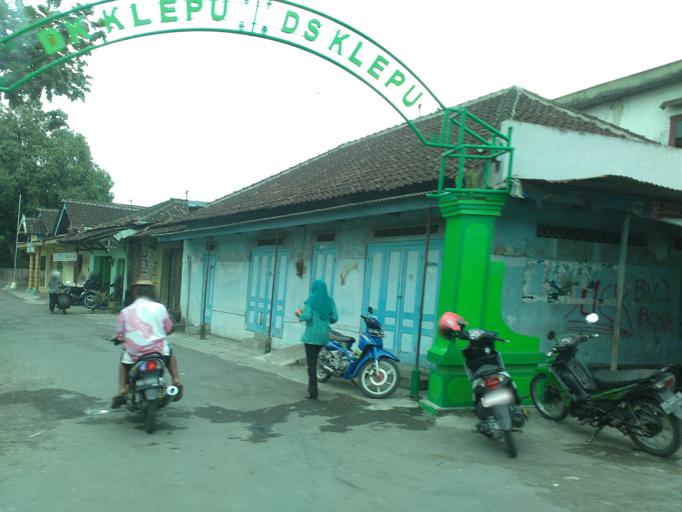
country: ID
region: Central Java
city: Ceper
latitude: -7.6625
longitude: 110.6698
